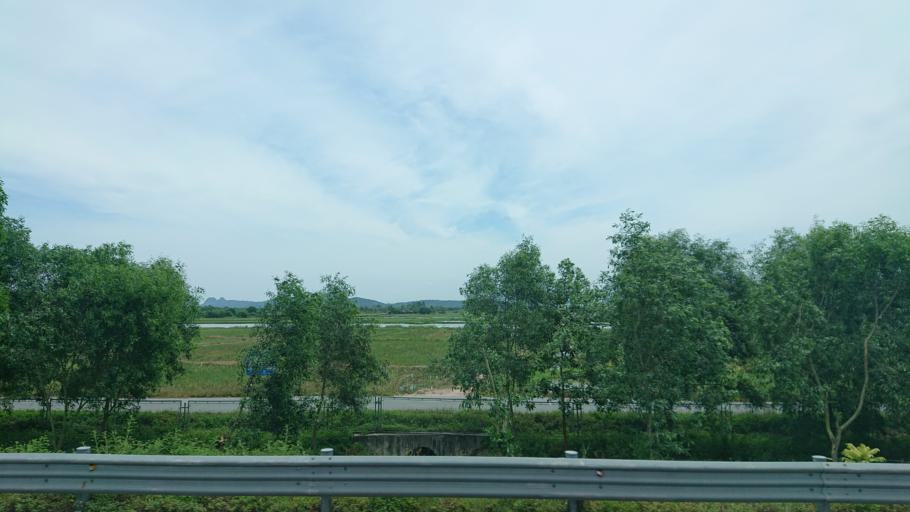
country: VN
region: Hai Phong
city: Tien Lang
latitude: 20.7710
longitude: 106.5896
